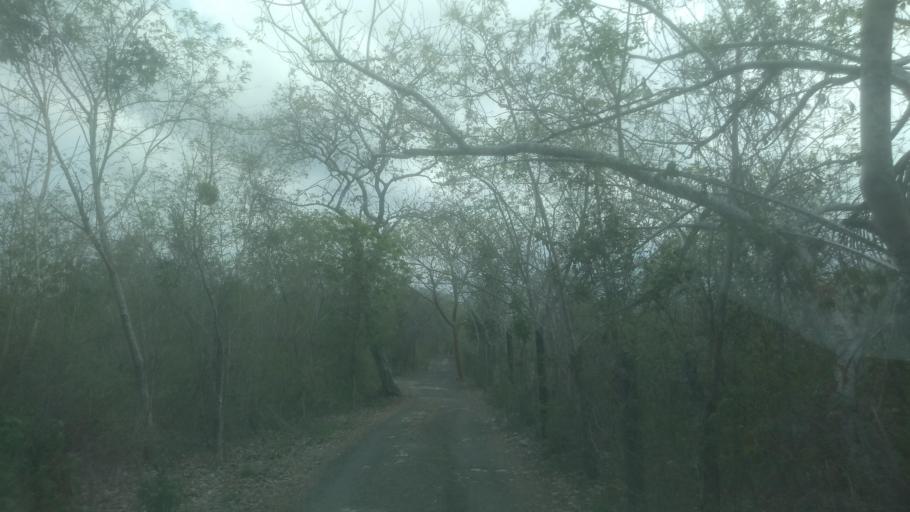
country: MX
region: Veracruz
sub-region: Emiliano Zapata
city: Plan del Rio
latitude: 19.3896
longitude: -96.6308
